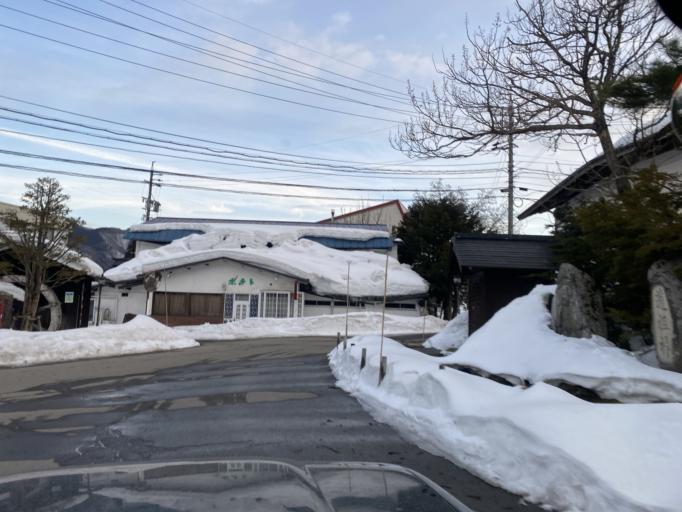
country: JP
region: Nagano
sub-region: Kitaazumi Gun
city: Hakuba
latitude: 36.7138
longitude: 137.8672
